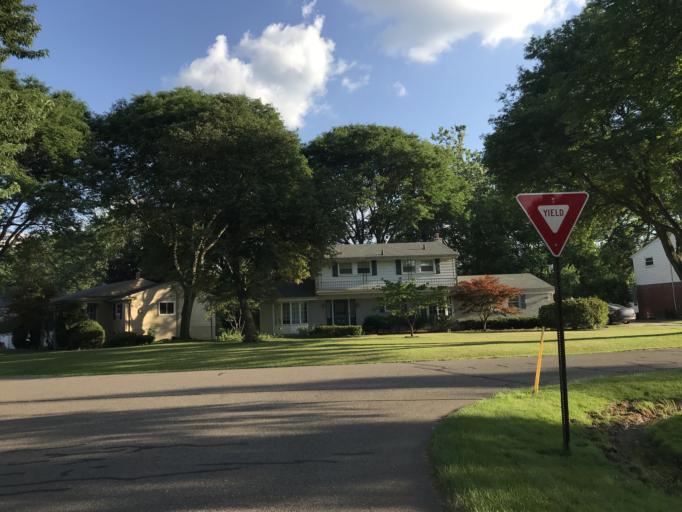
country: US
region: Michigan
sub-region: Oakland County
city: Farmington Hills
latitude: 42.4874
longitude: -83.3412
